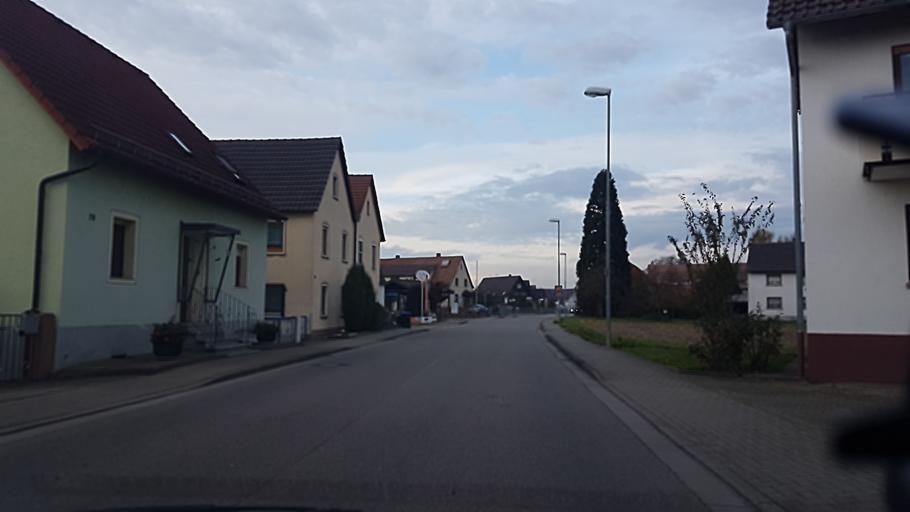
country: DE
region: Baden-Wuerttemberg
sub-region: Freiburg Region
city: Rust
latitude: 48.2344
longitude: 7.7125
